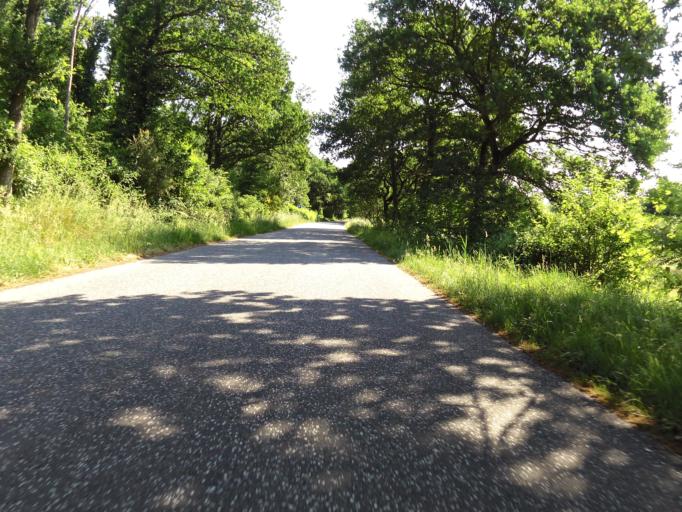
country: DK
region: Central Jutland
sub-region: Holstebro Kommune
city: Vinderup
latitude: 56.5678
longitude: 8.7707
